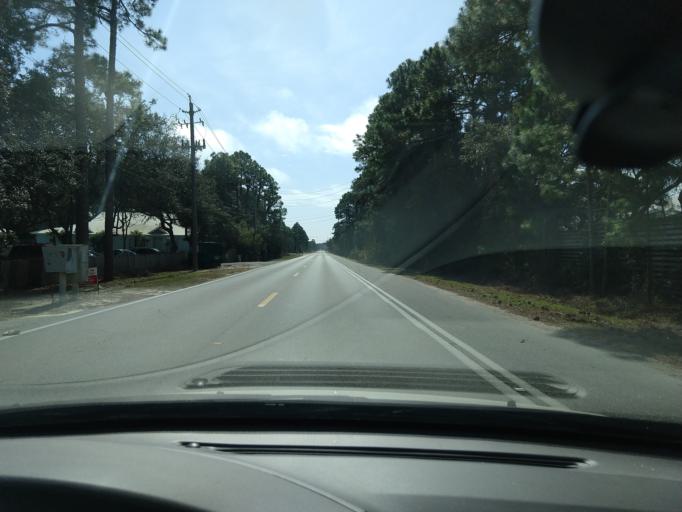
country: US
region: Florida
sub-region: Walton County
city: Miramar Beach
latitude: 30.3903
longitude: -86.3045
